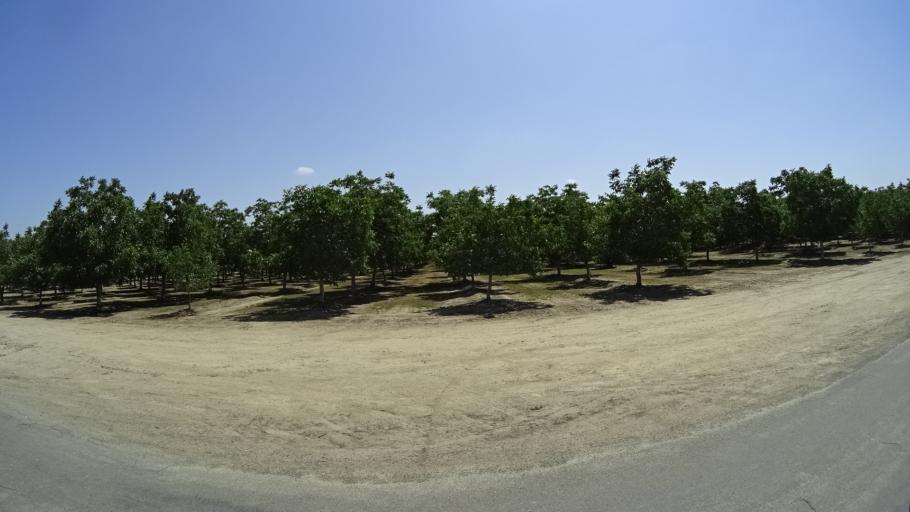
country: US
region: California
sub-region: Kings County
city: Home Garden
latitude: 36.3168
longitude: -119.6258
